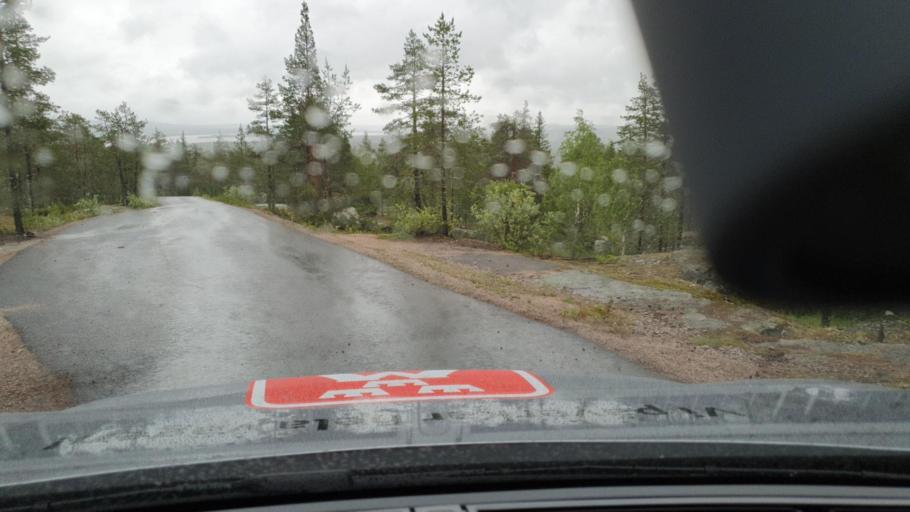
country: FI
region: Lapland
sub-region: Torniolaakso
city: Ylitornio
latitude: 66.3108
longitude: 23.6124
